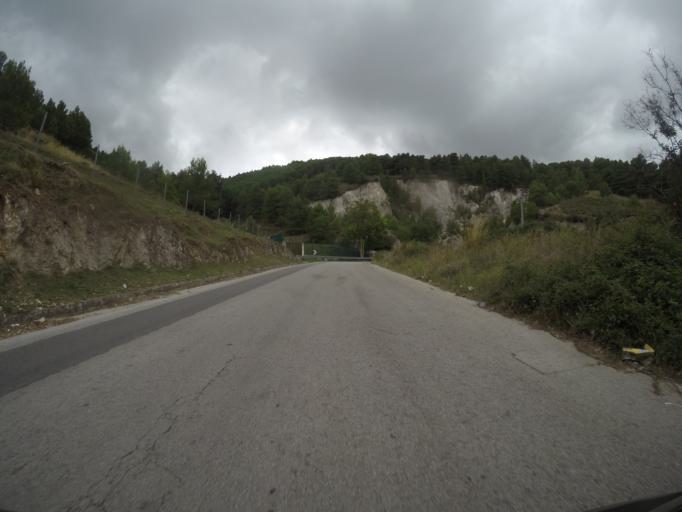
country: IT
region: Sicily
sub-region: Palermo
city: Montelepre
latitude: 38.1155
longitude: 13.1712
